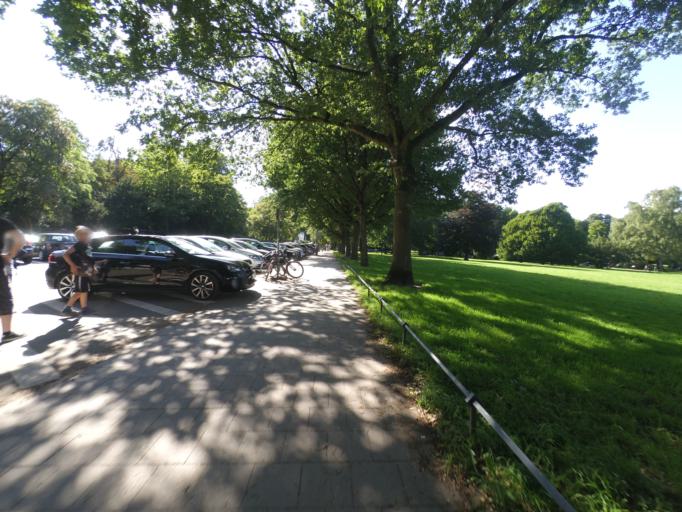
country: DE
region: Hamburg
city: Hamburg
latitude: 53.5735
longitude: 10.0015
